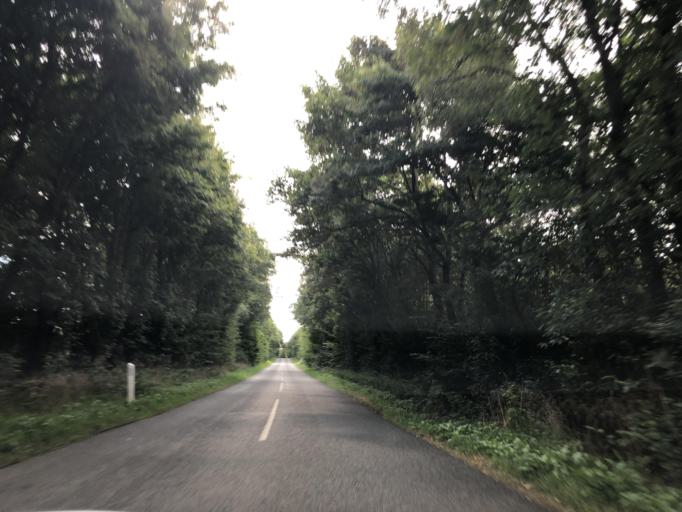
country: DK
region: North Denmark
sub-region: Vesthimmerland Kommune
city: Alestrup
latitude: 56.6024
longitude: 9.4331
